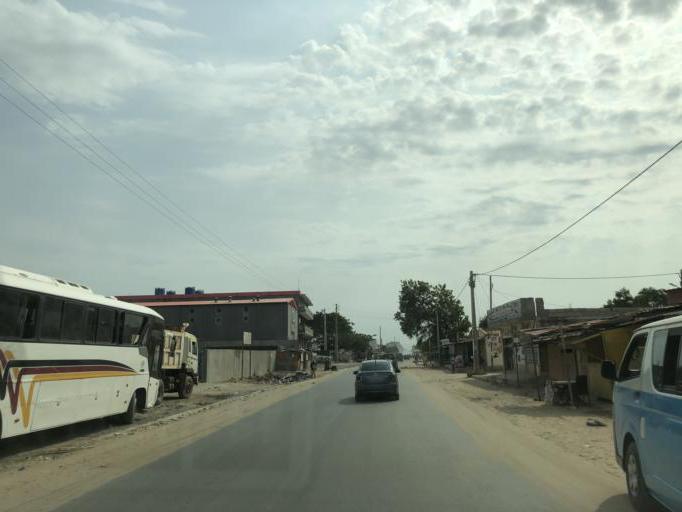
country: AO
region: Luanda
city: Luanda
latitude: -8.9023
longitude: 13.3477
